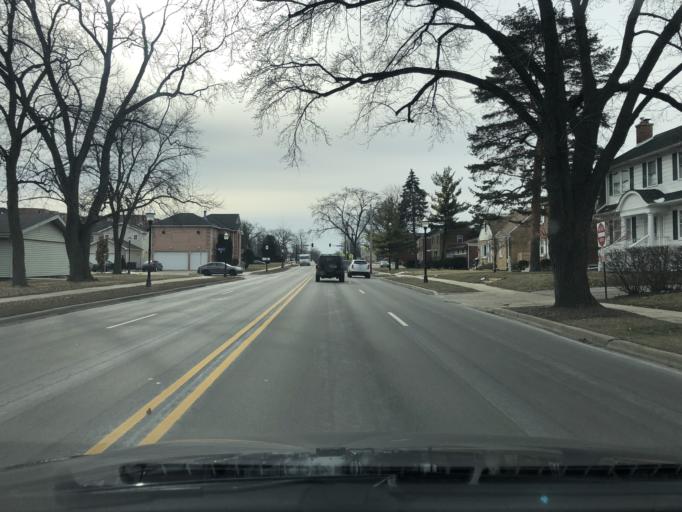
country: US
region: Illinois
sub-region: DuPage County
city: Bensenville
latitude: 41.9520
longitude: -87.9397
